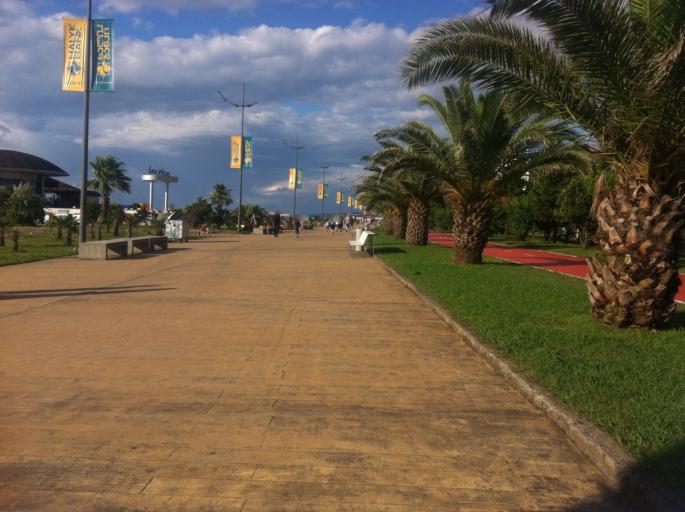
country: GE
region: Ajaria
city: Batumi
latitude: 41.6456
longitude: 41.6176
